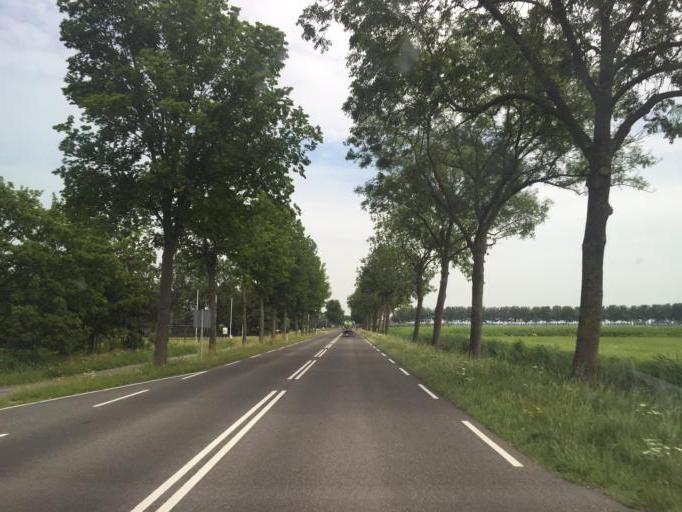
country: NL
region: North Holland
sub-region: Gemeente Beemster
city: Halfweg
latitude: 52.5969
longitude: 4.9423
